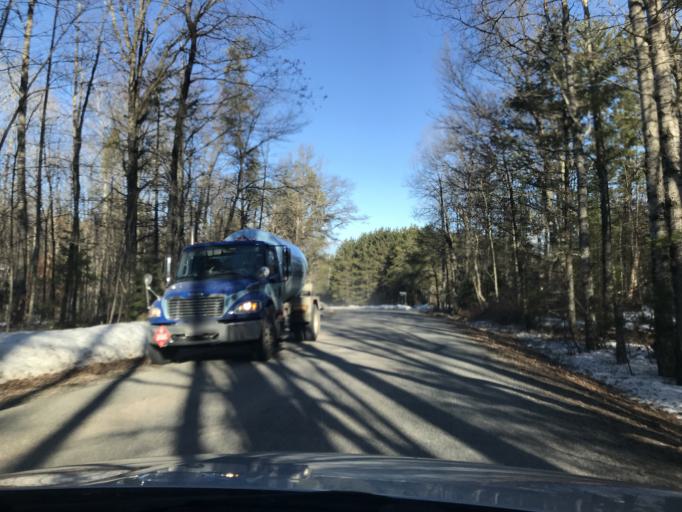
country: US
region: Wisconsin
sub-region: Marinette County
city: Niagara
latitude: 45.3917
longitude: -88.0536
